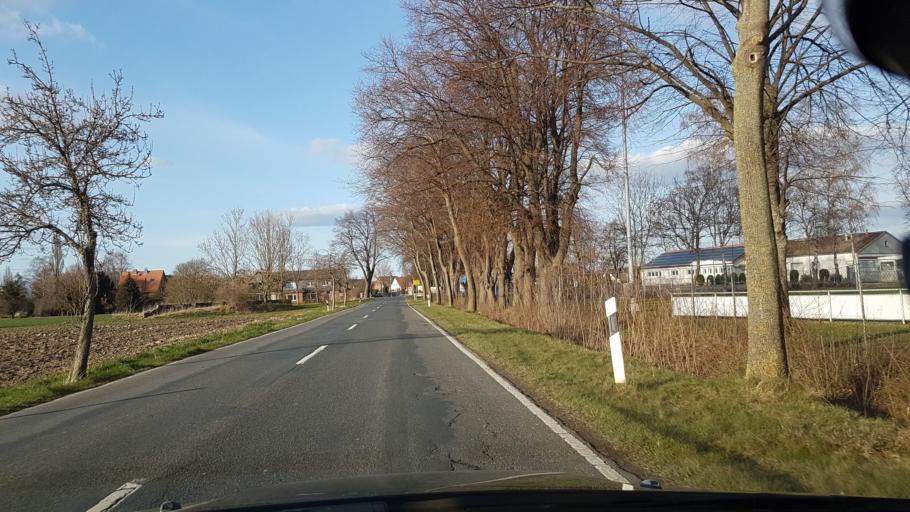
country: DE
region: Lower Saxony
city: Egestorf
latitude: 52.3143
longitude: 9.5475
